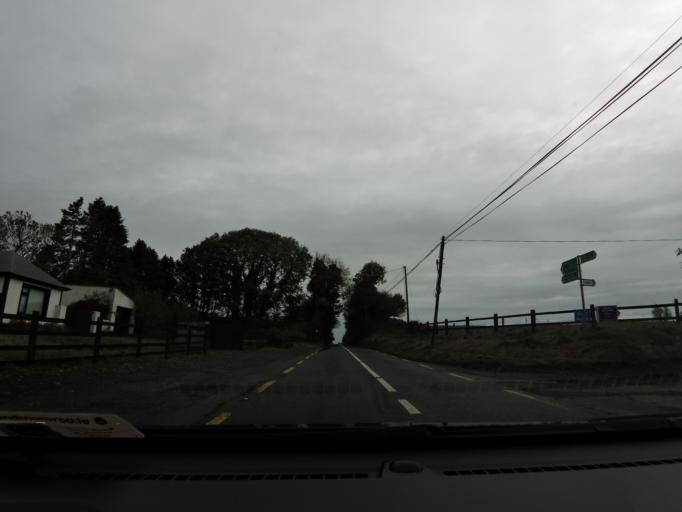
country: IE
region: Connaught
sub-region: County Galway
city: Tuam
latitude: 53.5805
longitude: -8.7816
